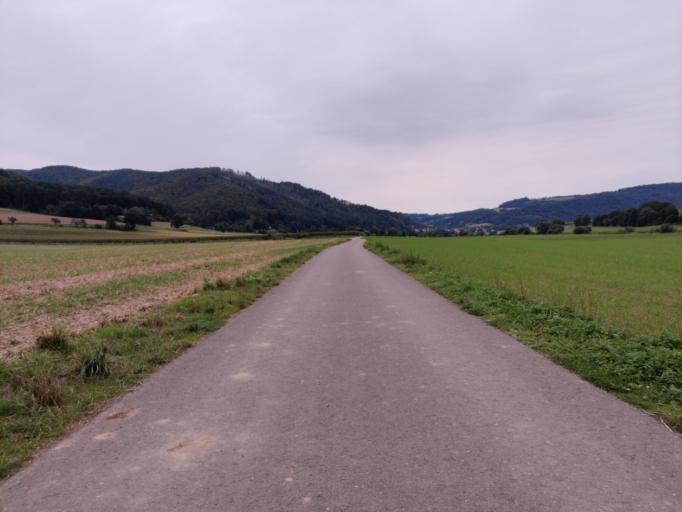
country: DE
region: Lower Saxony
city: Pegestorf
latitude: 51.9506
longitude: 9.5055
